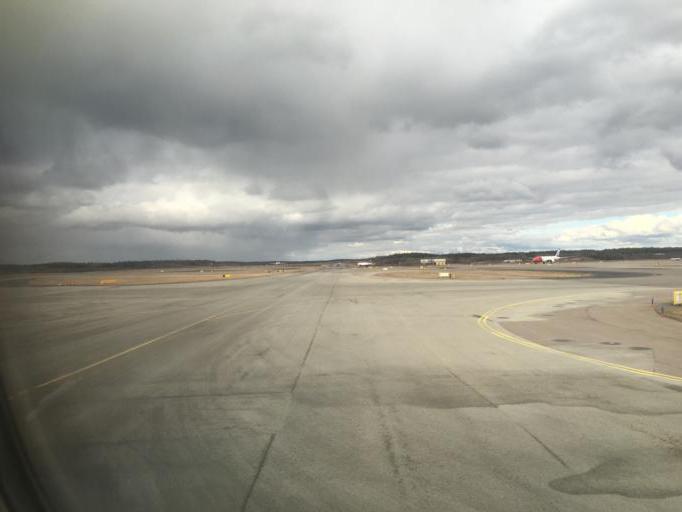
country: SE
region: Stockholm
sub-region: Sigtuna Kommun
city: Marsta
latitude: 59.6490
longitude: 17.9213
